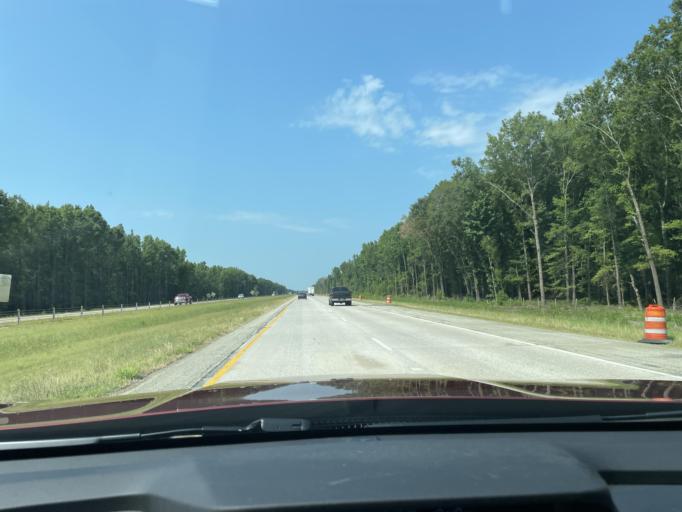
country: US
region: Arkansas
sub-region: White County
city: Searcy
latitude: 35.1674
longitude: -91.7738
